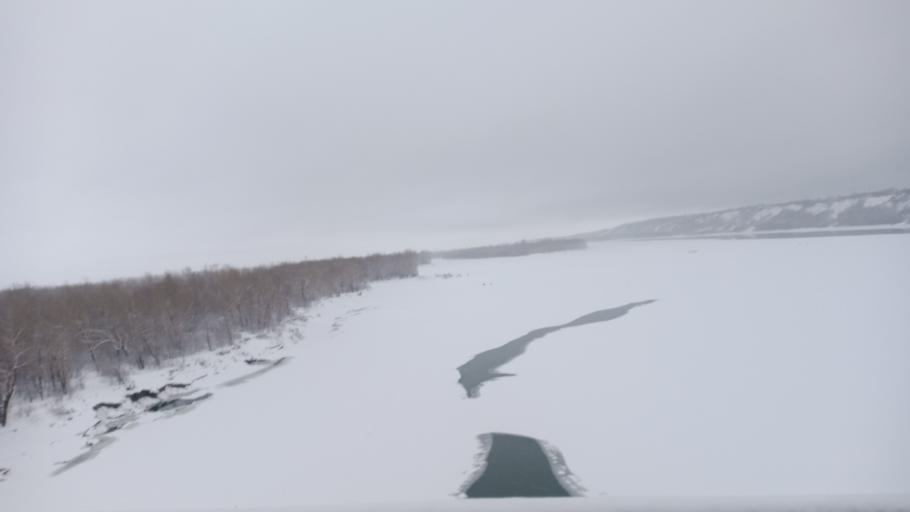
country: RU
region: Altai Krai
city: Zaton
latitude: 53.3223
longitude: 83.8062
